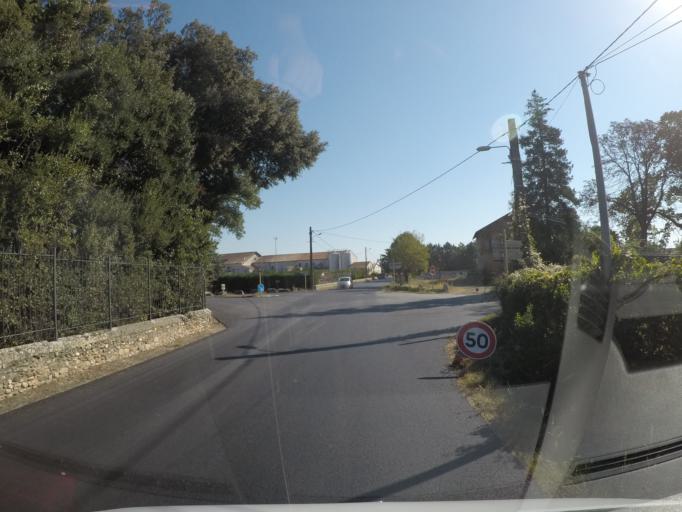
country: FR
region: Languedoc-Roussillon
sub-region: Departement du Gard
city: Ribaute-les-Tavernes
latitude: 44.0242
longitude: 4.0795
